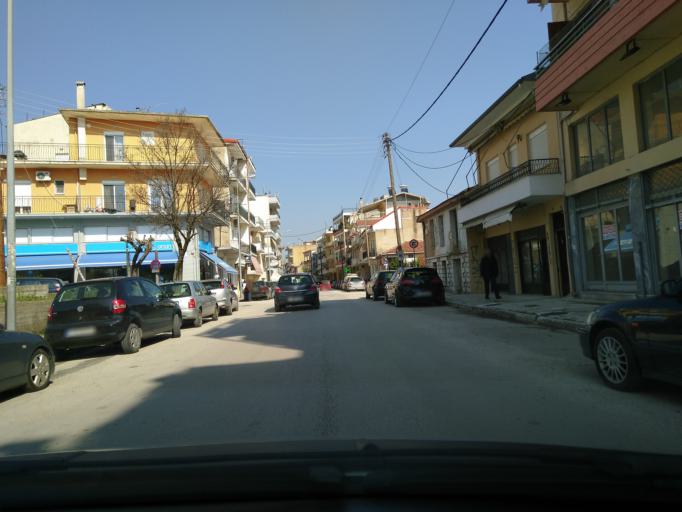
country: GR
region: Epirus
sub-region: Nomos Ioanninon
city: Ioannina
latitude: 39.6746
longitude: 20.8440
